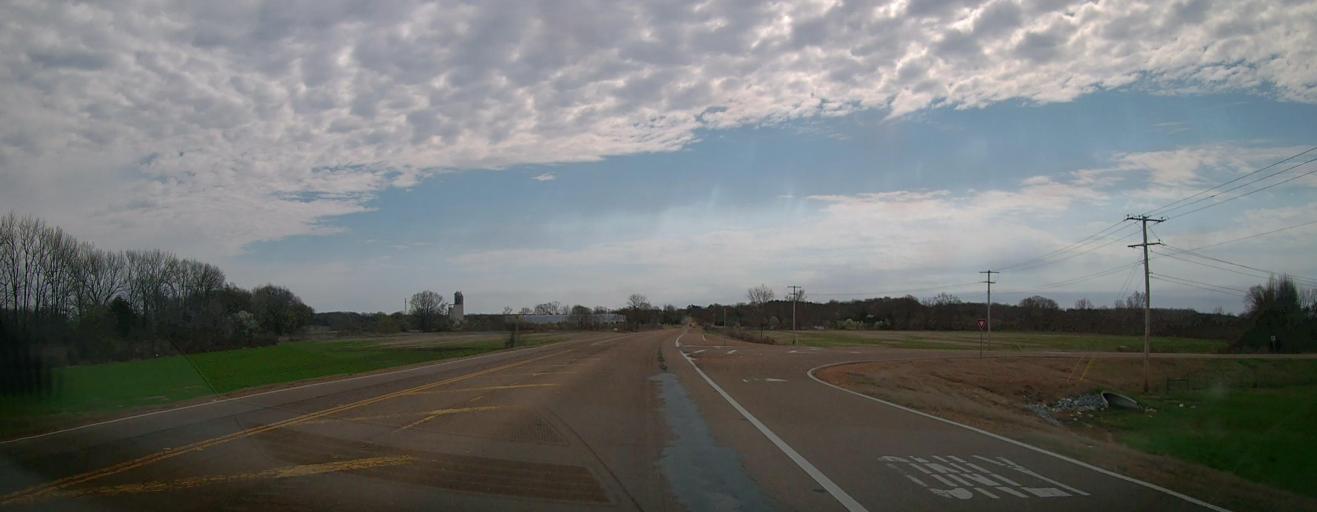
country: US
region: Mississippi
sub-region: Marshall County
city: Byhalia
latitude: 34.8678
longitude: -89.6676
